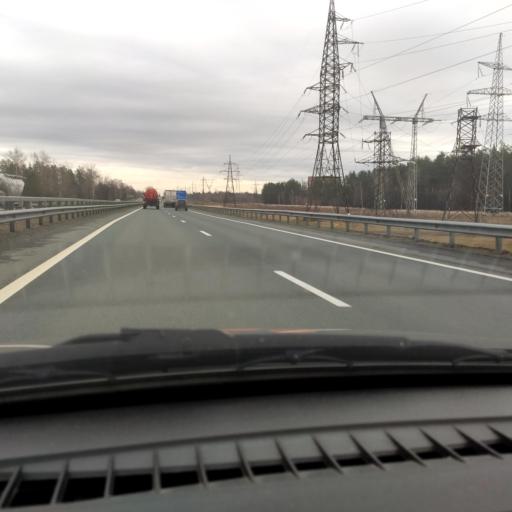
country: RU
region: Samara
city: Pribrezhnyy
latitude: 53.5185
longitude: 49.8202
